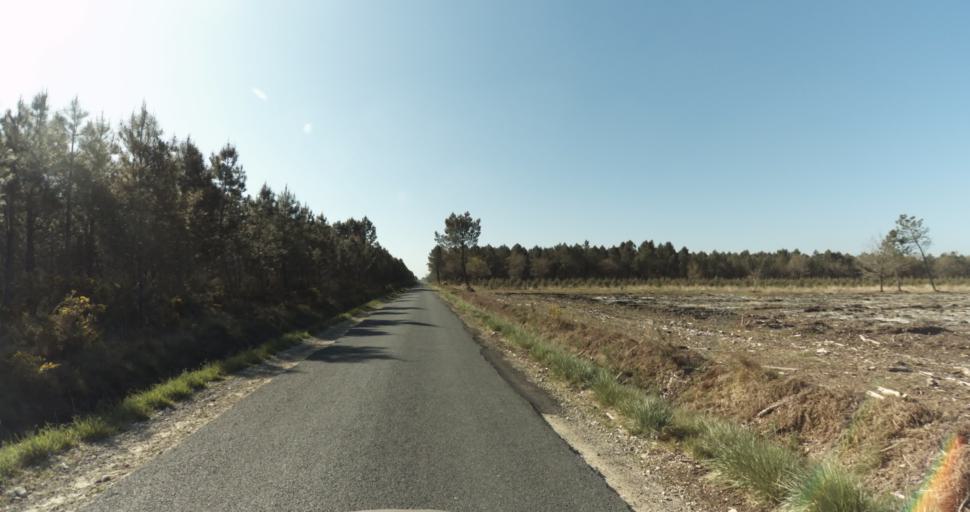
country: FR
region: Aquitaine
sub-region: Departement de la Gironde
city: Marcheprime
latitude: 44.7887
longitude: -0.8634
